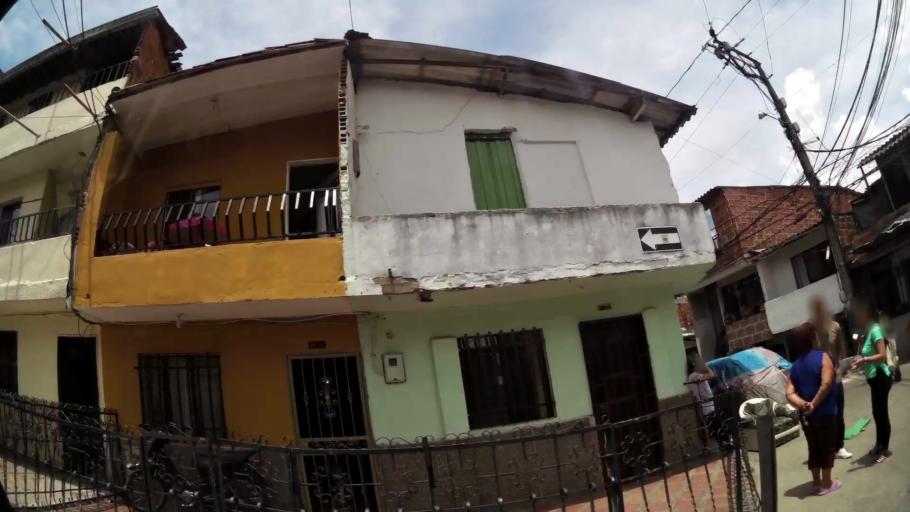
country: CO
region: Antioquia
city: Bello
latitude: 6.3369
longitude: -75.5523
